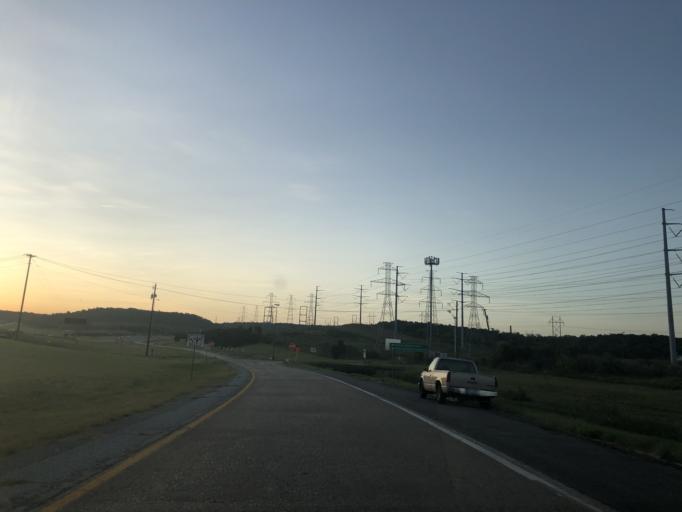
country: US
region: Texas
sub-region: Dallas County
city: Duncanville
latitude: 32.6699
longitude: -96.9725
